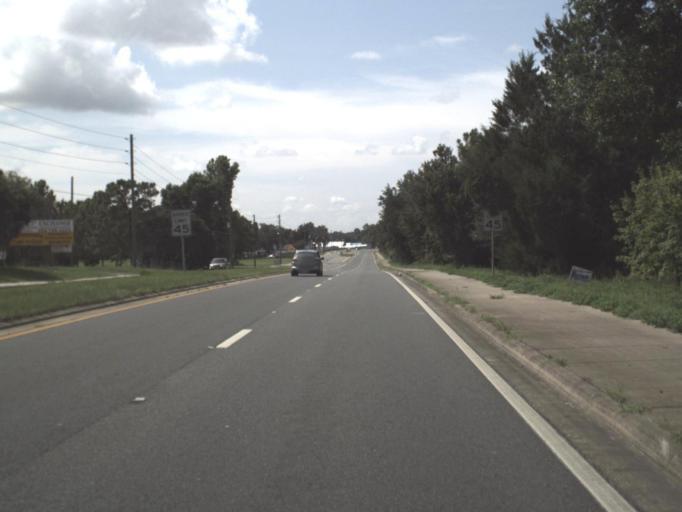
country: US
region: Florida
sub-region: Citrus County
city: Inverness Highlands South
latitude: 28.8032
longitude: -82.3103
